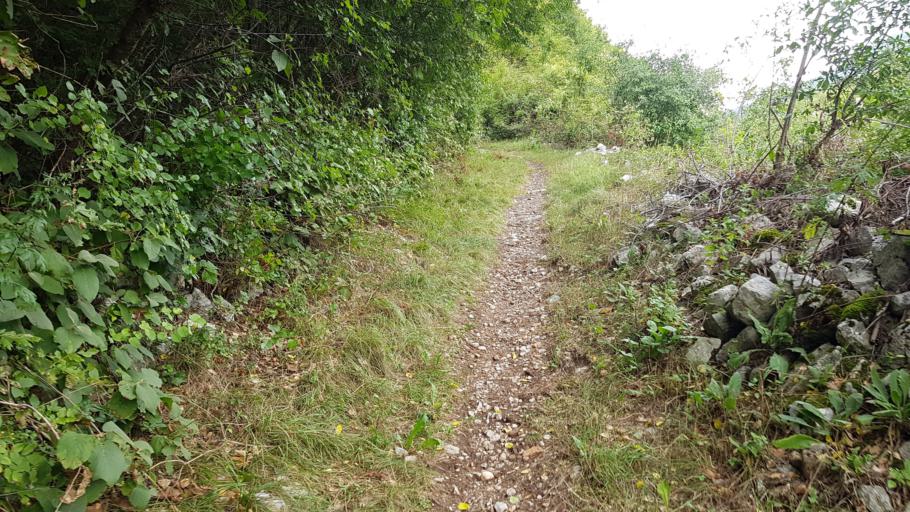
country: IT
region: Trentino-Alto Adige
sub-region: Provincia di Trento
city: Cavedine
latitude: 46.0083
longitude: 10.9765
